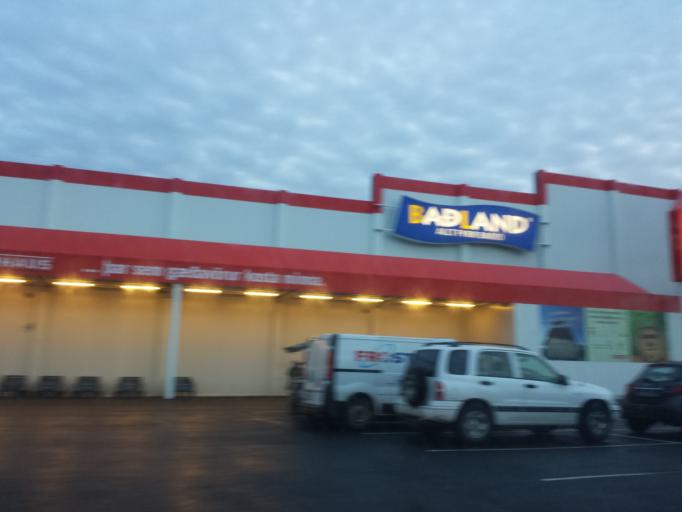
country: IS
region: Capital Region
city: Mosfellsbaer
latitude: 64.1412
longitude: -21.7536
